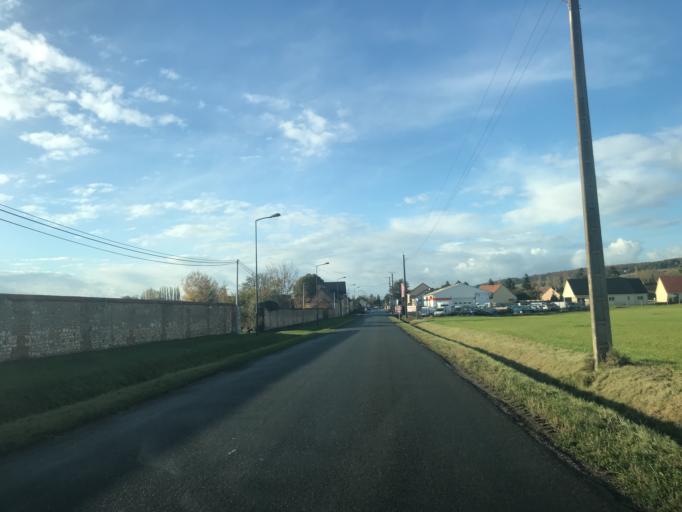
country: FR
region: Haute-Normandie
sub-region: Departement de l'Eure
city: Saint-Aubin-sur-Gaillon
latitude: 49.0936
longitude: 1.2849
